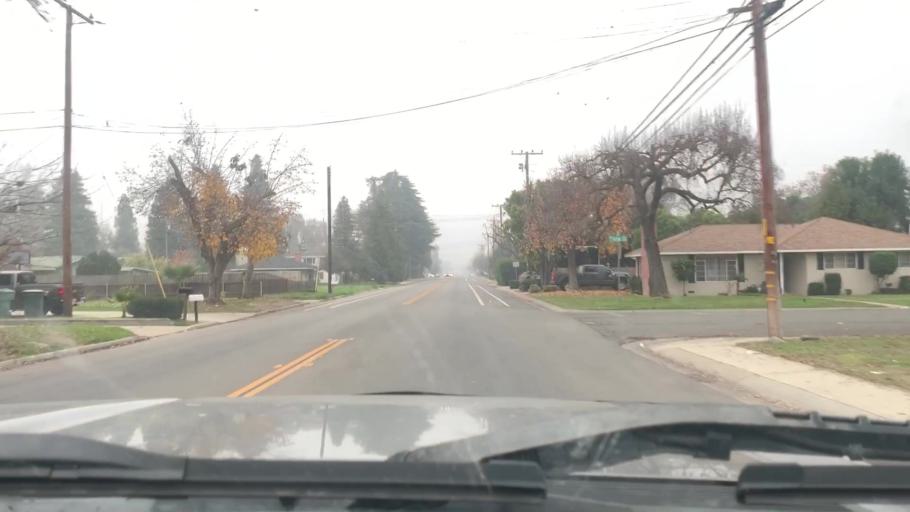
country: US
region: California
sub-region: Tulare County
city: Visalia
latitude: 36.3195
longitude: -119.3054
